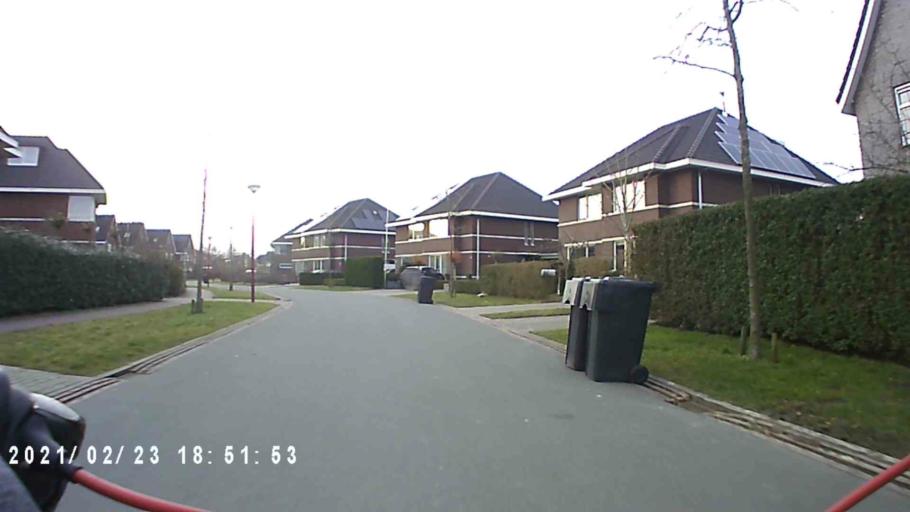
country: NL
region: Groningen
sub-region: Gemeente Winsum
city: Winsum
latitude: 53.3365
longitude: 6.5306
